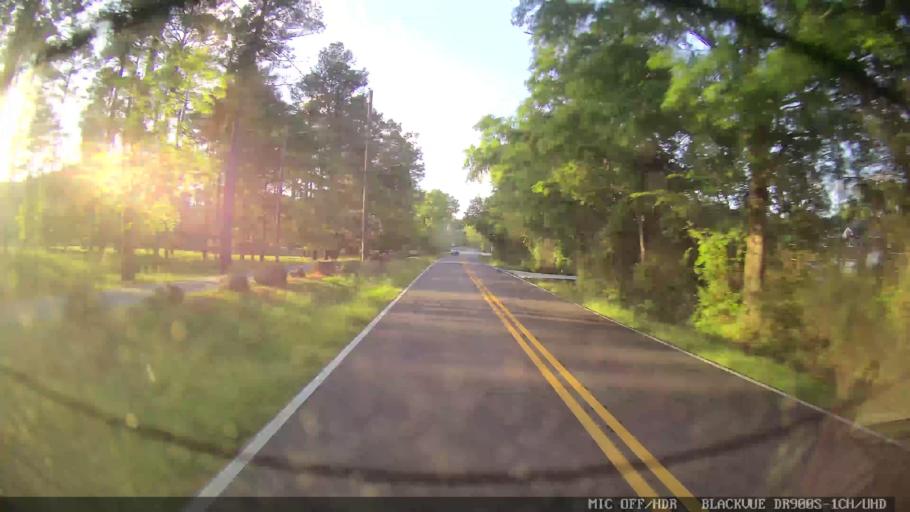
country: US
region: Georgia
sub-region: Bartow County
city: Cartersville
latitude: 34.1382
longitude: -84.8089
